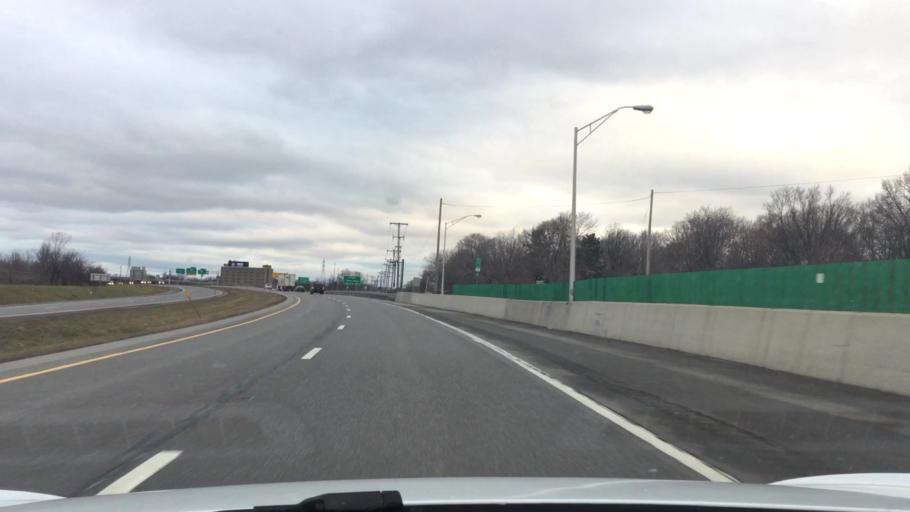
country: US
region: New York
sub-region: Niagara County
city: Lewiston
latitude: 43.1470
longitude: -79.0234
